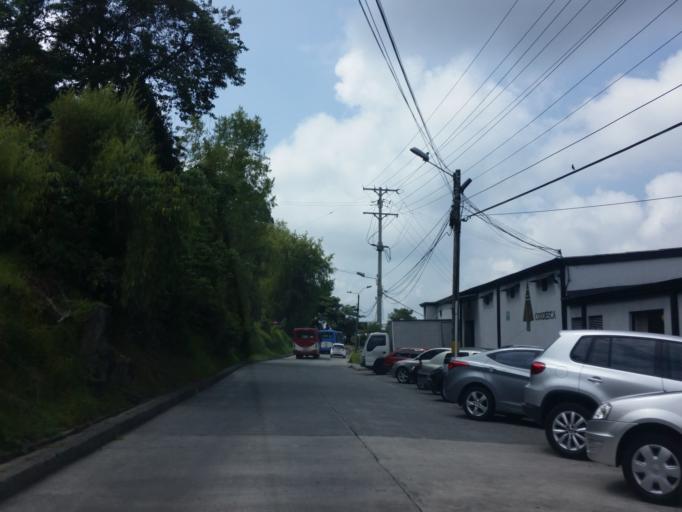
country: CO
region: Caldas
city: Manizales
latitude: 5.0575
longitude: -75.5291
